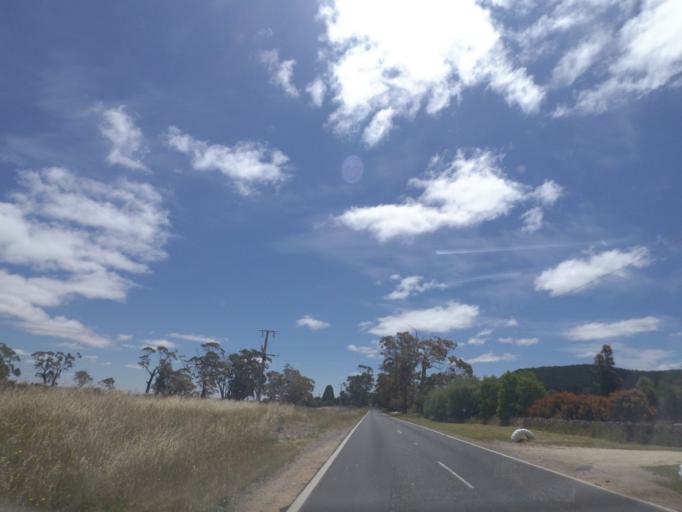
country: AU
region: Victoria
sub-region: Mount Alexander
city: Castlemaine
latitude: -37.2778
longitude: 144.1493
